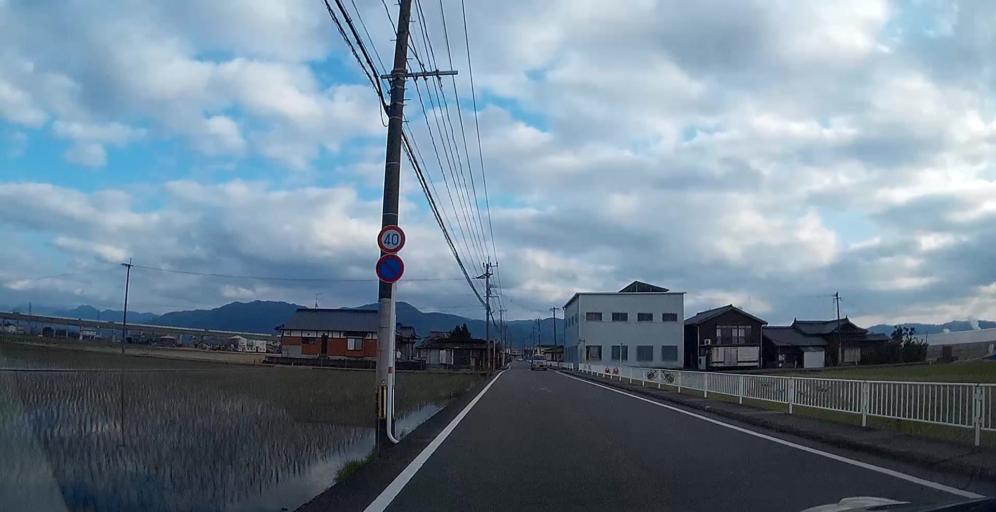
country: JP
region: Kumamoto
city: Yatsushiro
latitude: 32.5437
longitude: 130.6210
